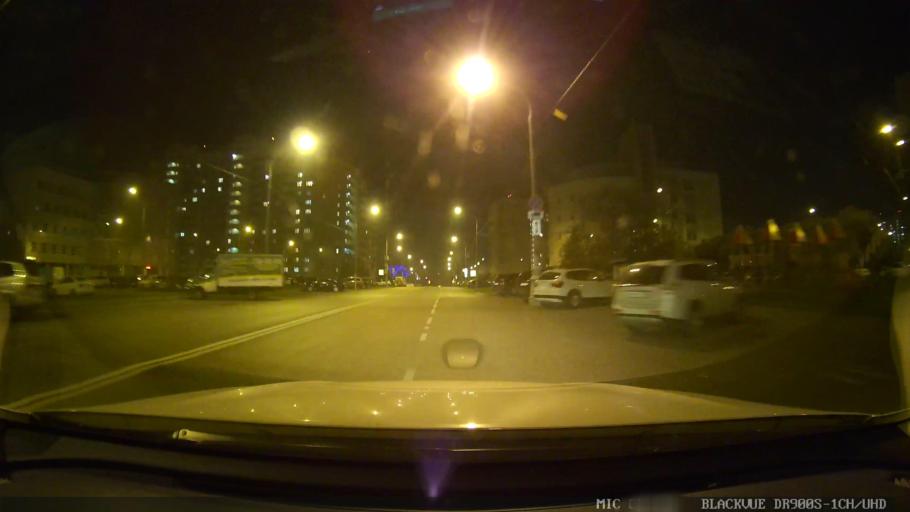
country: RU
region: Moskovskaya
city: Shcherbinka
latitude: 55.5036
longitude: 37.5821
